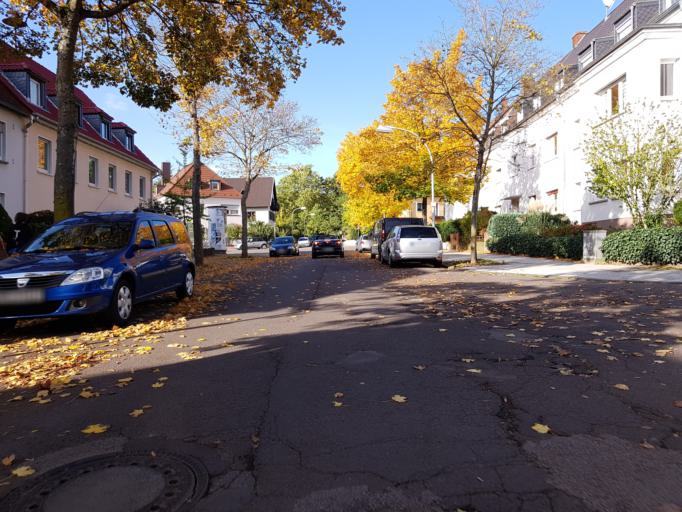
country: DE
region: Saarland
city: Saarbrucken
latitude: 49.2495
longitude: 6.9911
